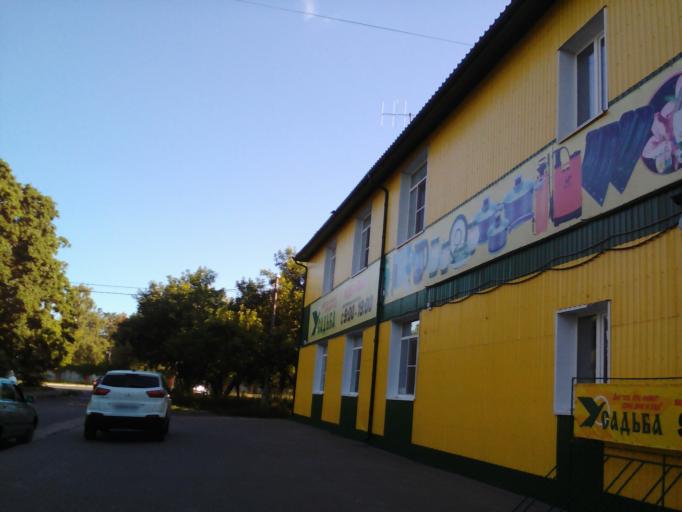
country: RU
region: Kursk
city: Voroshnevo
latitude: 51.6689
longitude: 36.0807
